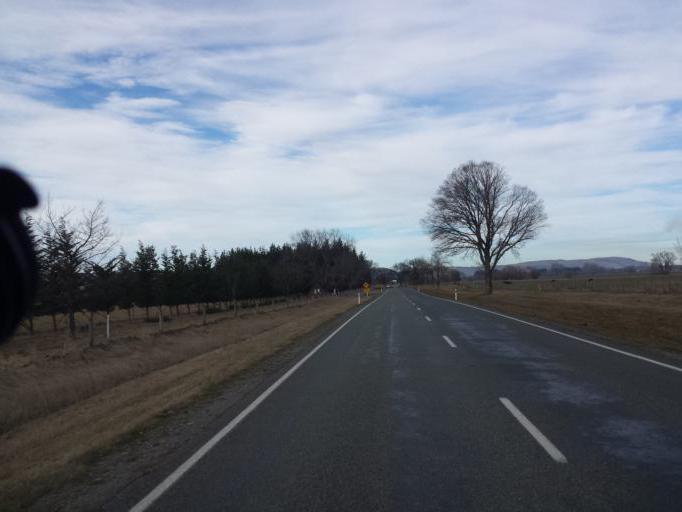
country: NZ
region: Canterbury
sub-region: Timaru District
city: Pleasant Point
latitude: -44.0768
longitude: 170.7998
